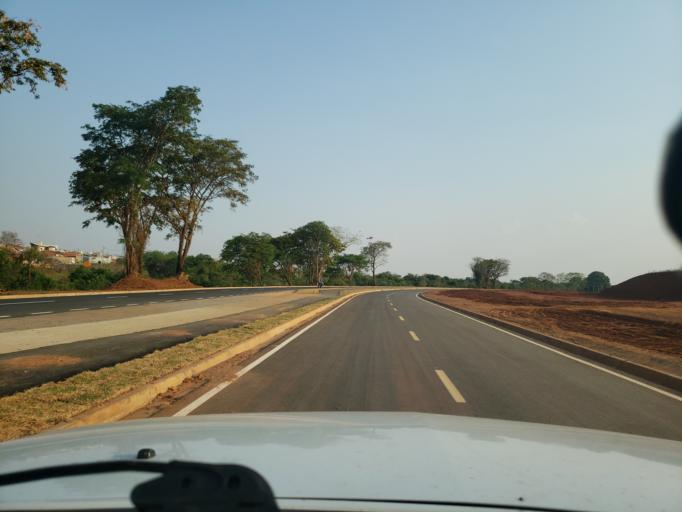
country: BR
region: Sao Paulo
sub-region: Moji-Guacu
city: Mogi-Gaucu
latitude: -22.3174
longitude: -46.9464
